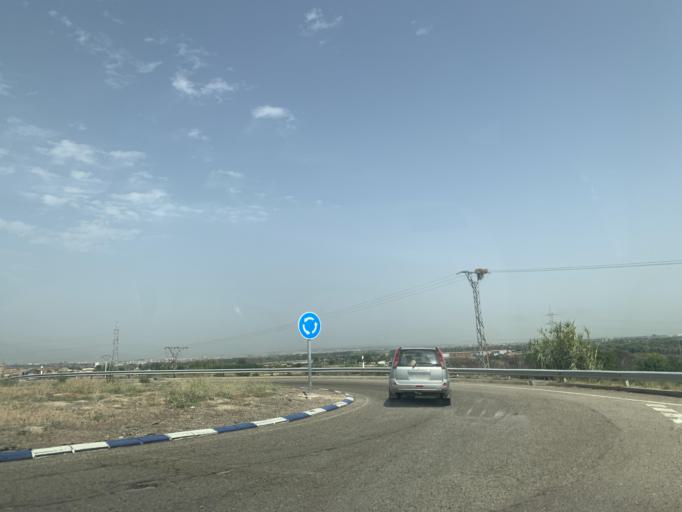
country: ES
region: Aragon
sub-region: Provincia de Zaragoza
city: Puebla de Alfinden
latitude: 41.5976
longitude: -0.8053
